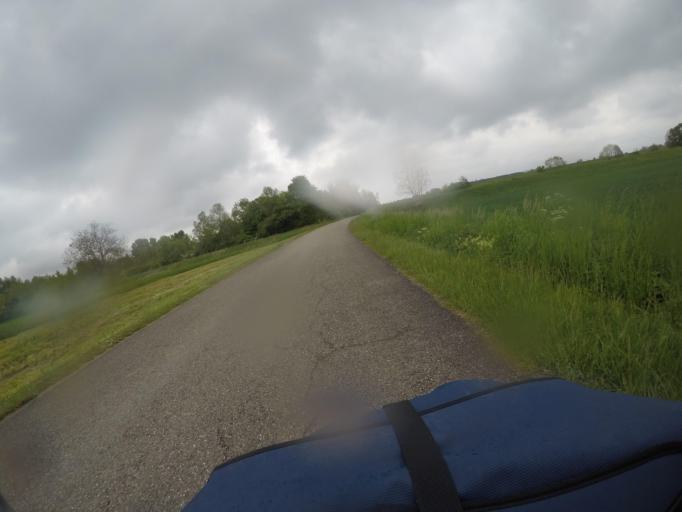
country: DE
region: Baden-Wuerttemberg
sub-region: Karlsruhe Region
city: Hugelsheim
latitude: 48.8212
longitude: 8.0985
